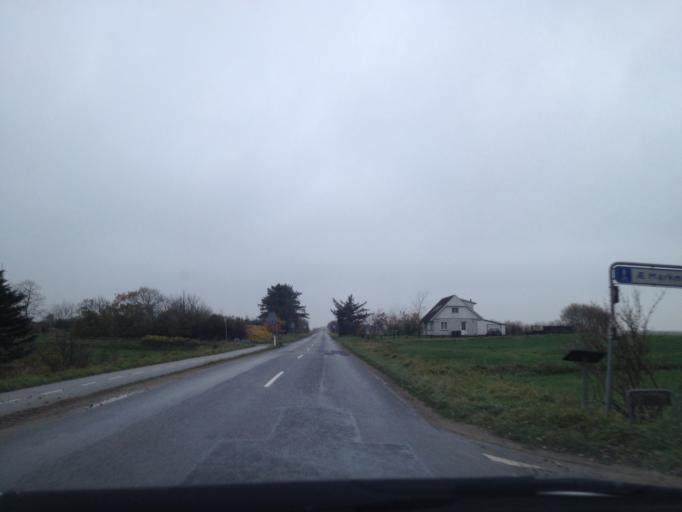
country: DK
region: South Denmark
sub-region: Tonder Kommune
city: Sherrebek
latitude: 55.1160
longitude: 8.7472
